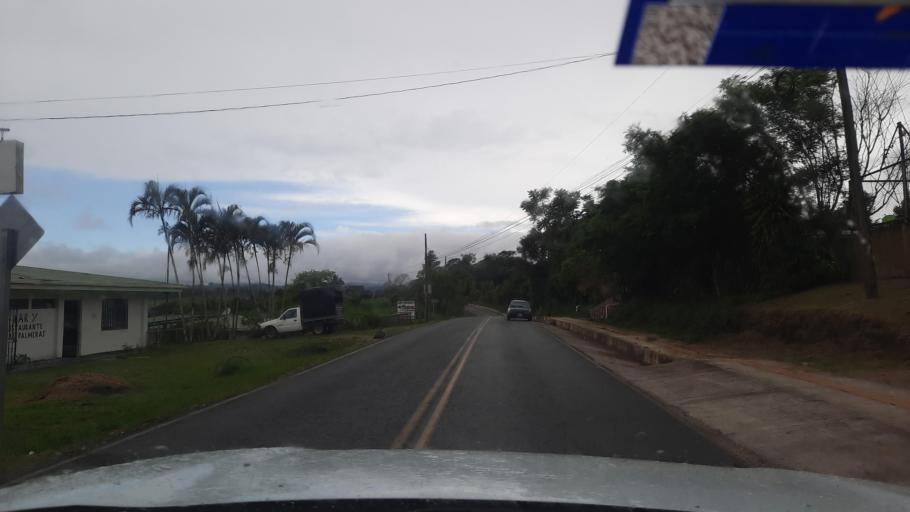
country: PA
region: Chiriqui
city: Rio Sereno
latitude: 8.8178
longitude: -82.8634
